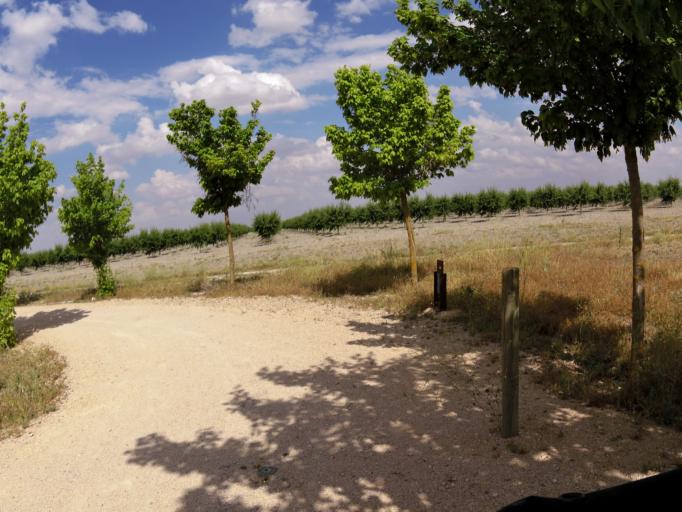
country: ES
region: Castille-La Mancha
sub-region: Provincia de Albacete
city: Albacete
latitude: 38.9552
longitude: -1.9790
